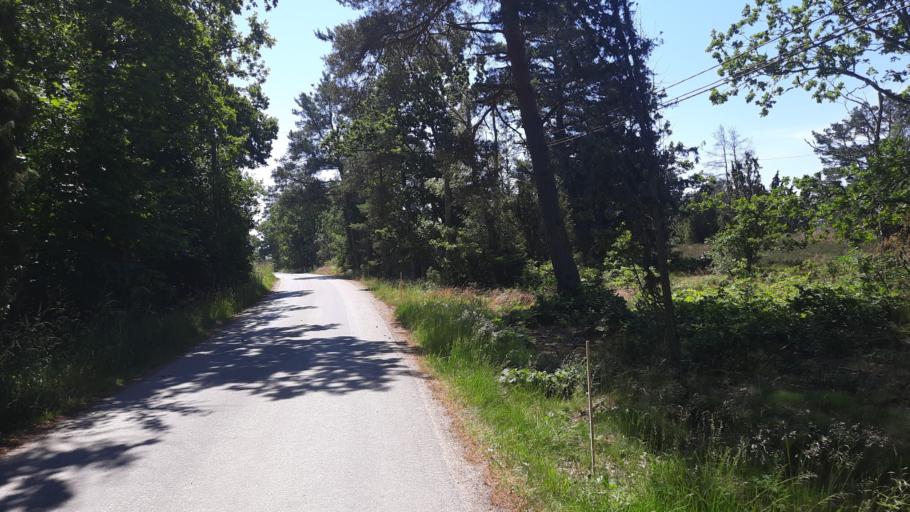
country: SE
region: Blekinge
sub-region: Karlskrona Kommun
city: Jaemjoe
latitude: 56.1492
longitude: 15.7692
